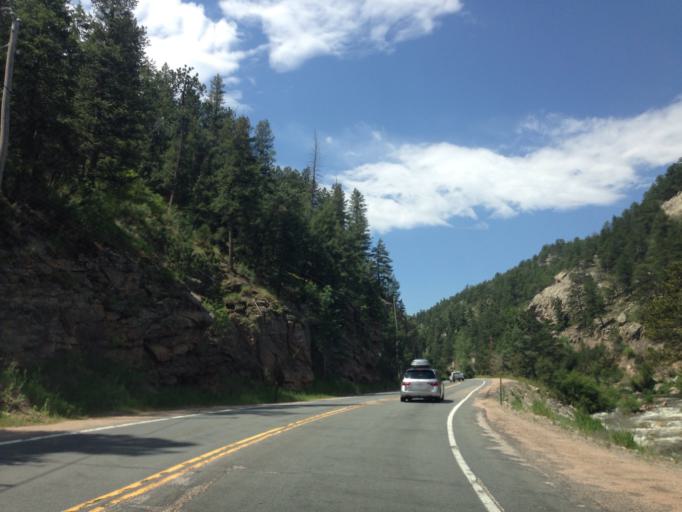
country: US
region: Colorado
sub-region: Larimer County
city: Estes Park
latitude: 40.4057
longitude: -105.4136
